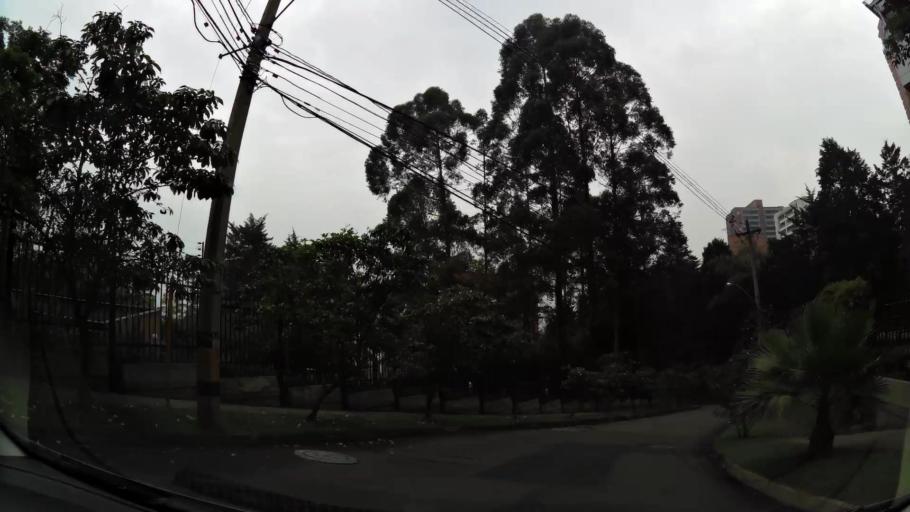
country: CO
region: Antioquia
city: Envigado
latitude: 6.2024
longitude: -75.5544
